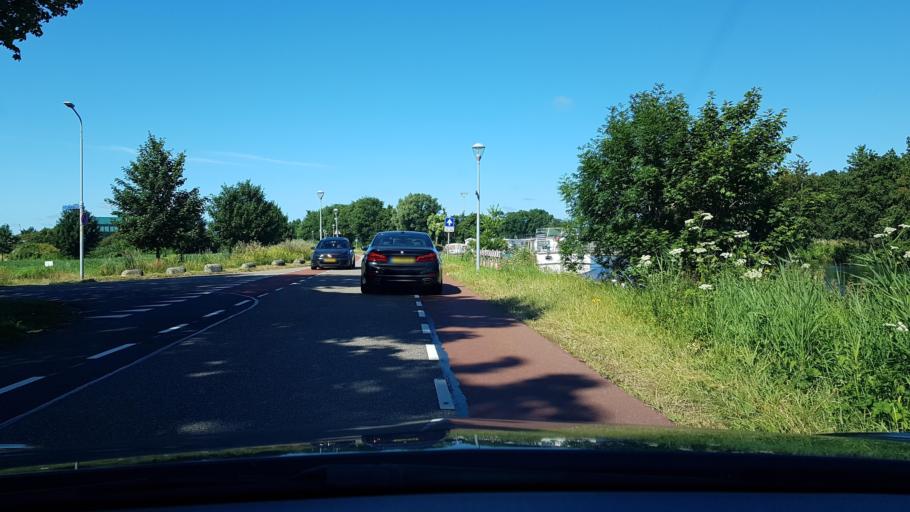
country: NL
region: North Holland
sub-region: Gemeente Heemstede
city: Heemstede
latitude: 52.3380
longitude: 4.6330
